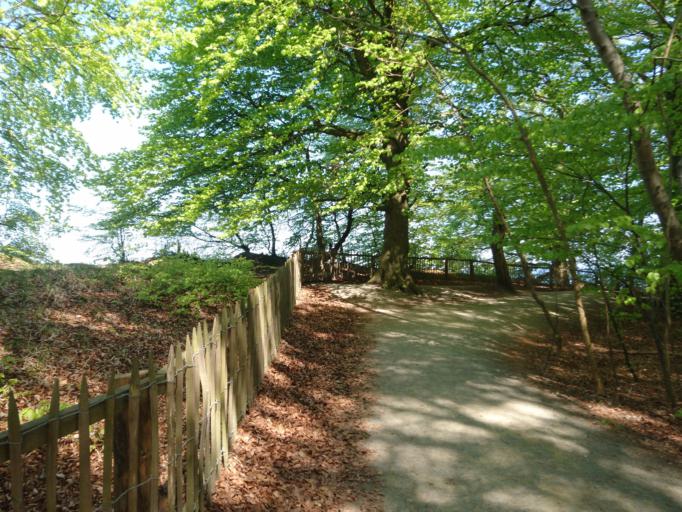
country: DE
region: Mecklenburg-Vorpommern
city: Sassnitz
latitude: 54.5710
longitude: 13.6641
